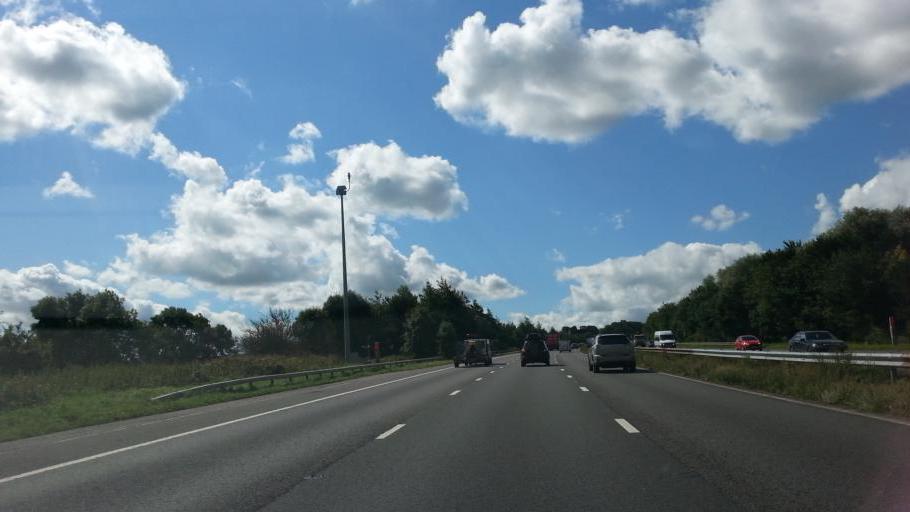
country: GB
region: England
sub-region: Leicestershire
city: Markfield
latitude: 52.7233
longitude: -1.2826
